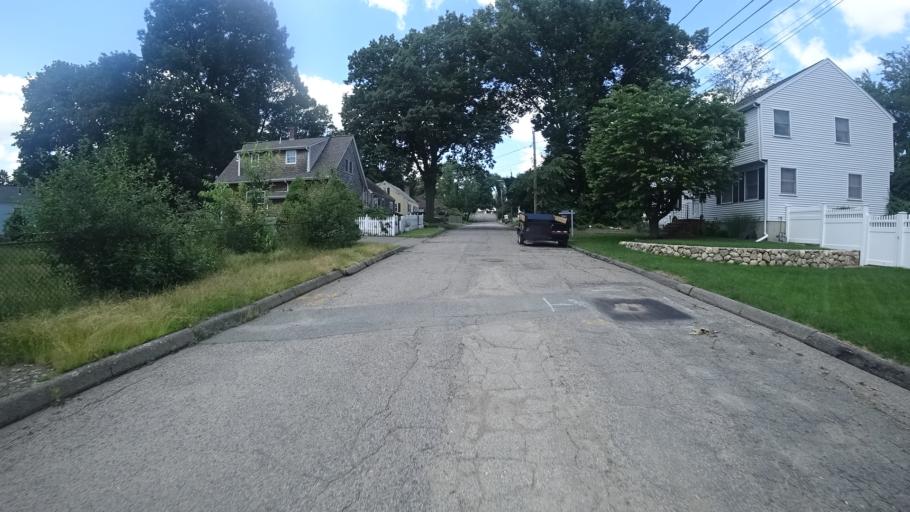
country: US
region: Massachusetts
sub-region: Norfolk County
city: Dedham
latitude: 42.2587
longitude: -71.1753
